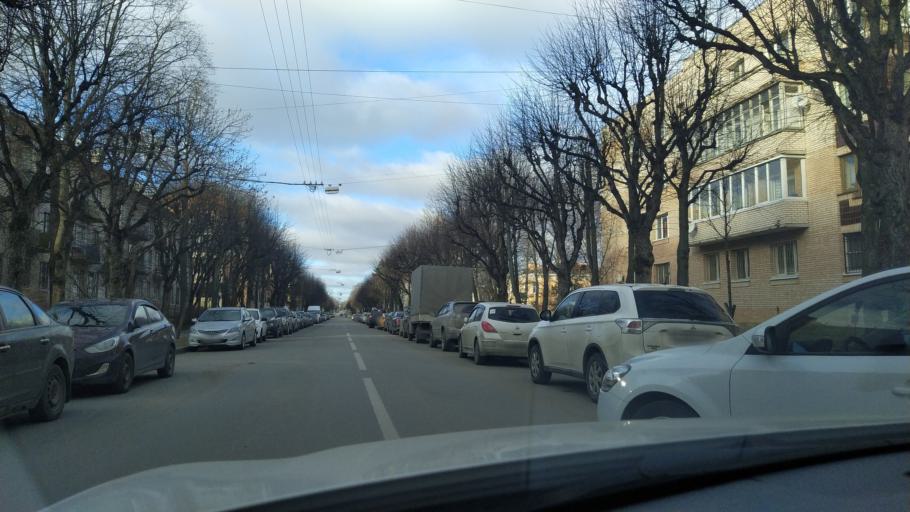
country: RU
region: St.-Petersburg
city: Pushkin
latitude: 59.7194
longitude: 30.4184
